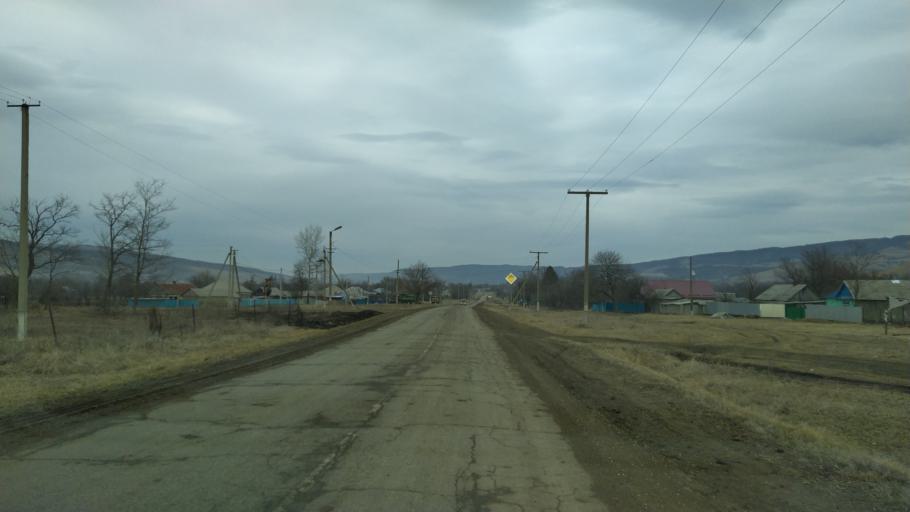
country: RU
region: Krasnodarskiy
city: Peredovaya
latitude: 44.1133
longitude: 41.4544
